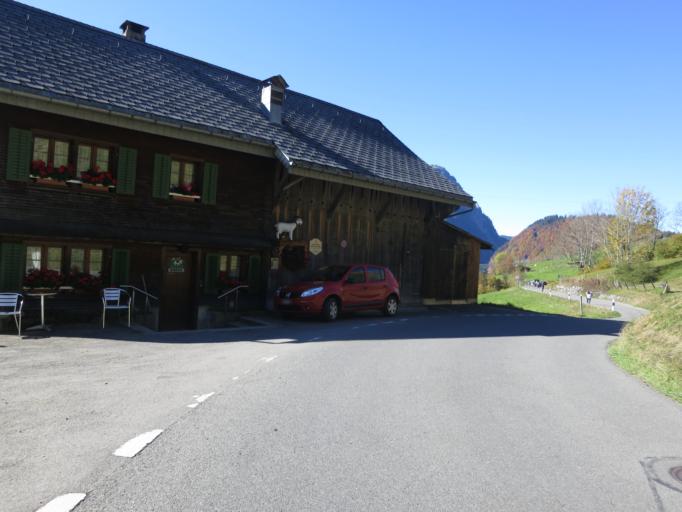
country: CH
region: Schwyz
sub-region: Bezirk March
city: Vorderthal
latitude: 47.0935
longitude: 8.9306
